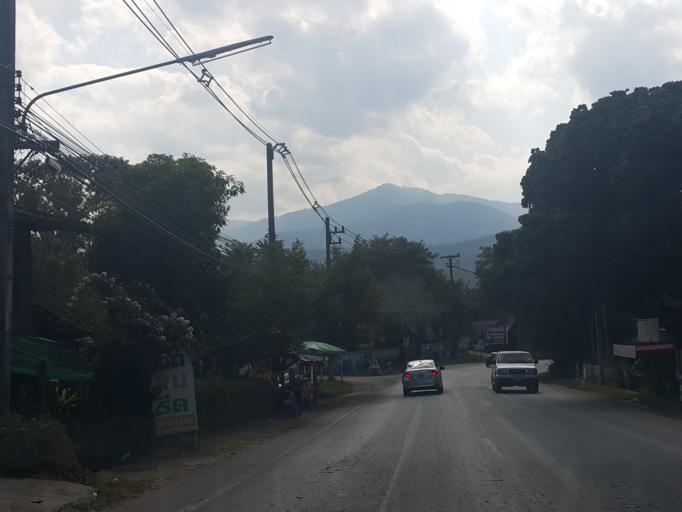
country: TH
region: Chiang Mai
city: Chiang Mai
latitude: 18.9162
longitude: 98.9089
